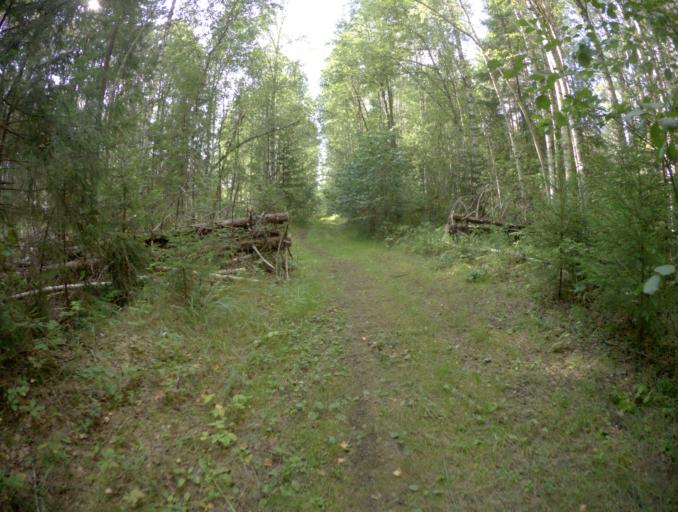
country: RU
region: Vladimir
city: Sobinka
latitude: 55.9128
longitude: 40.1079
